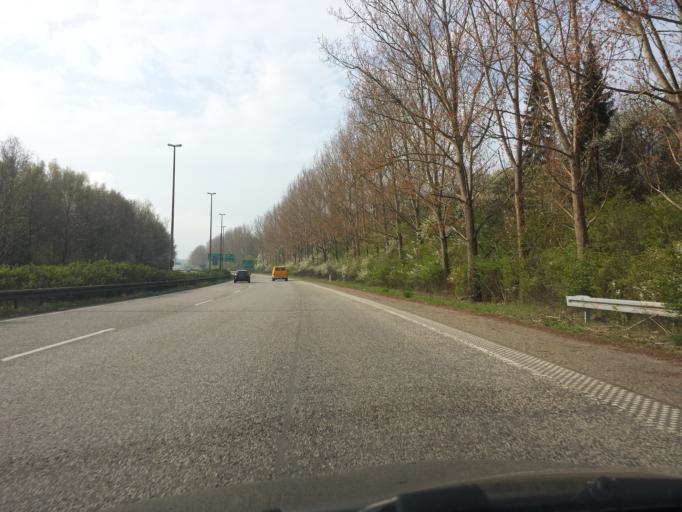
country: DK
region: Capital Region
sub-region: Ballerup Kommune
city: Ballerup
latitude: 55.7190
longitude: 12.3650
